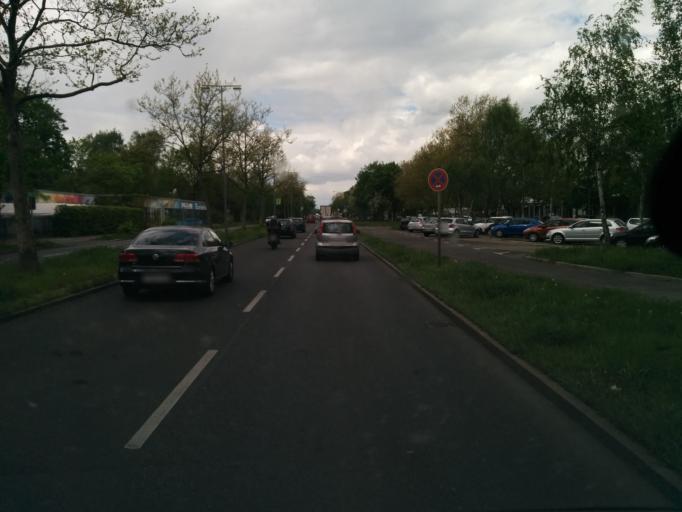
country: DE
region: Berlin
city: Staaken
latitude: 52.5230
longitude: 13.1493
